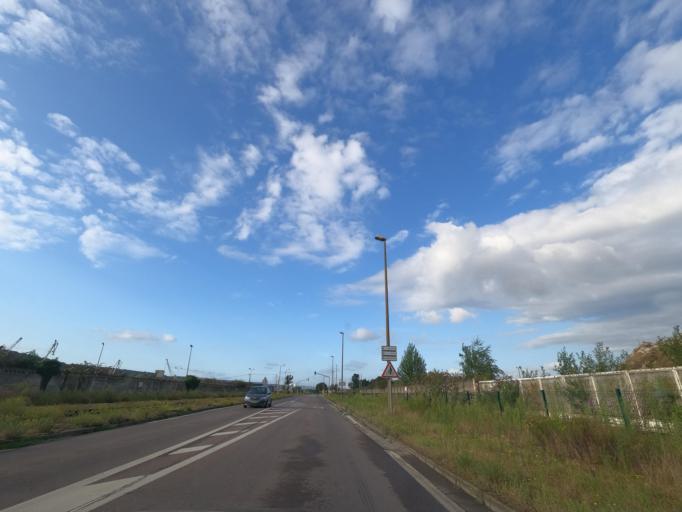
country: FR
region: Haute-Normandie
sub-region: Departement de la Seine-Maritime
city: Petit-Couronne
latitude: 49.3828
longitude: 1.0154
